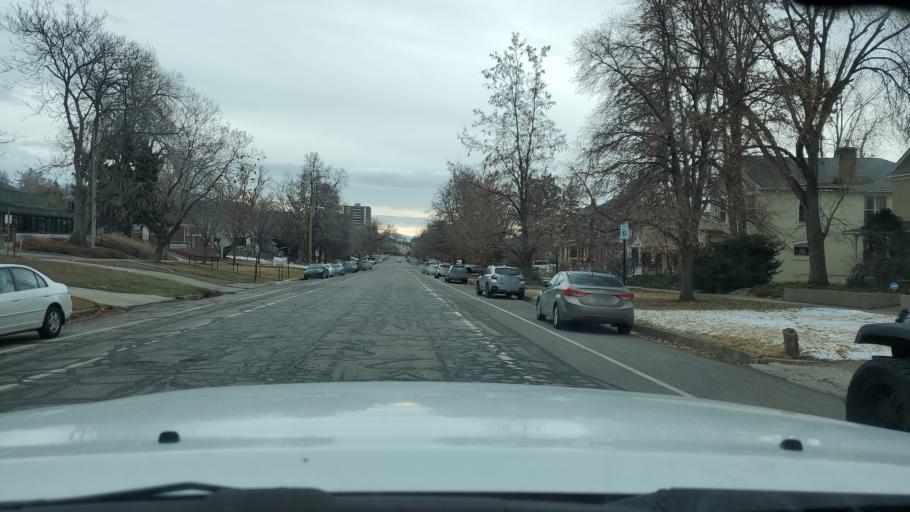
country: US
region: Utah
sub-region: Salt Lake County
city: Salt Lake City
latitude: 40.7644
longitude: -111.8636
